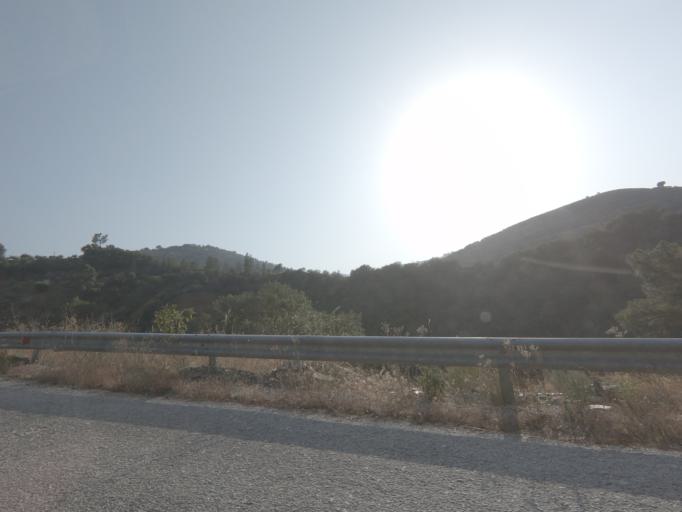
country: PT
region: Viseu
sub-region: Tabuaco
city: Tabuaco
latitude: 41.1265
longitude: -7.5487
